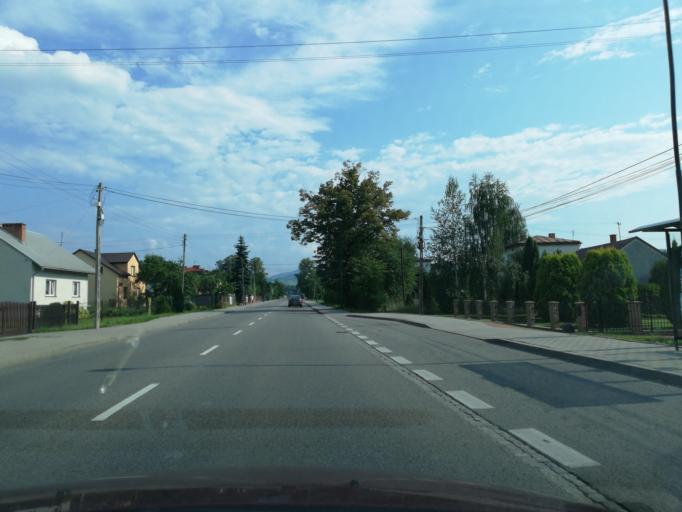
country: PL
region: Lesser Poland Voivodeship
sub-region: Powiat nowosadecki
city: Nawojowa
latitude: 49.5731
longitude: 20.7343
